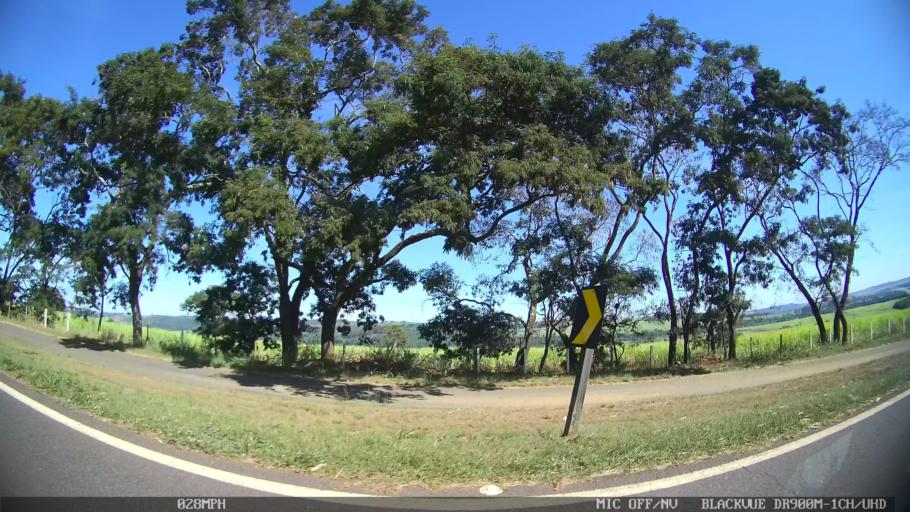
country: BR
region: Sao Paulo
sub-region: Santa Rita Do Passa Quatro
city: Santa Rita do Passa Quatro
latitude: -21.7566
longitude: -47.5652
